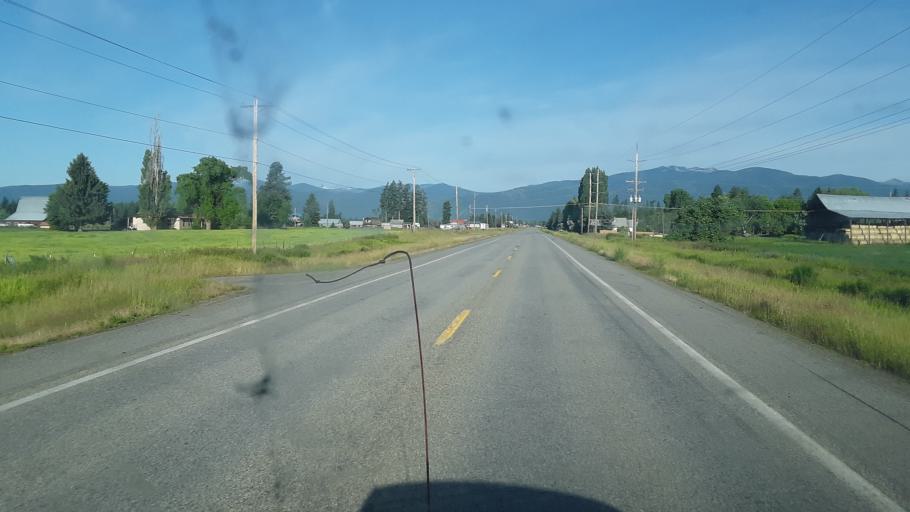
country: US
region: Idaho
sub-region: Boundary County
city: Bonners Ferry
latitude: 48.7315
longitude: -116.2729
